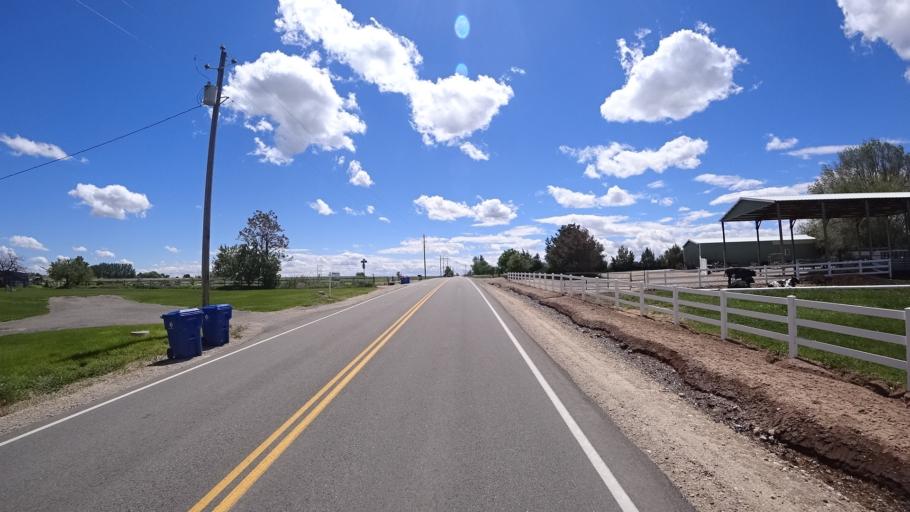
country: US
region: Idaho
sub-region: Ada County
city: Meridian
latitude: 43.5725
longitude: -116.4537
